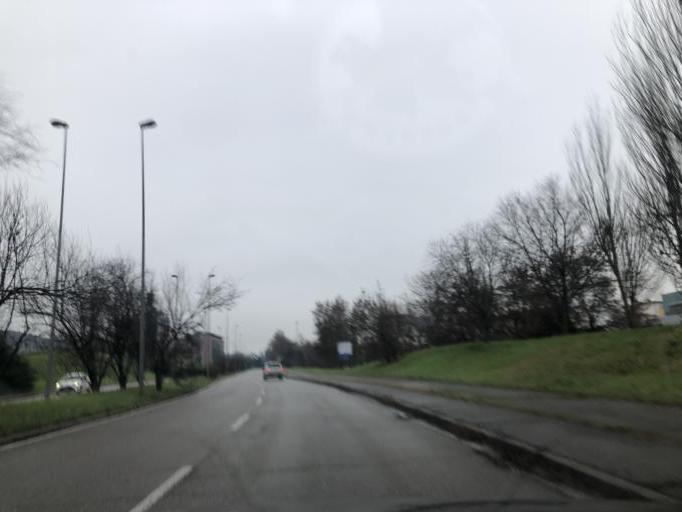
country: IT
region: Emilia-Romagna
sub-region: Provincia di Modena
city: Modena
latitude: 44.6405
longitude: 10.9011
